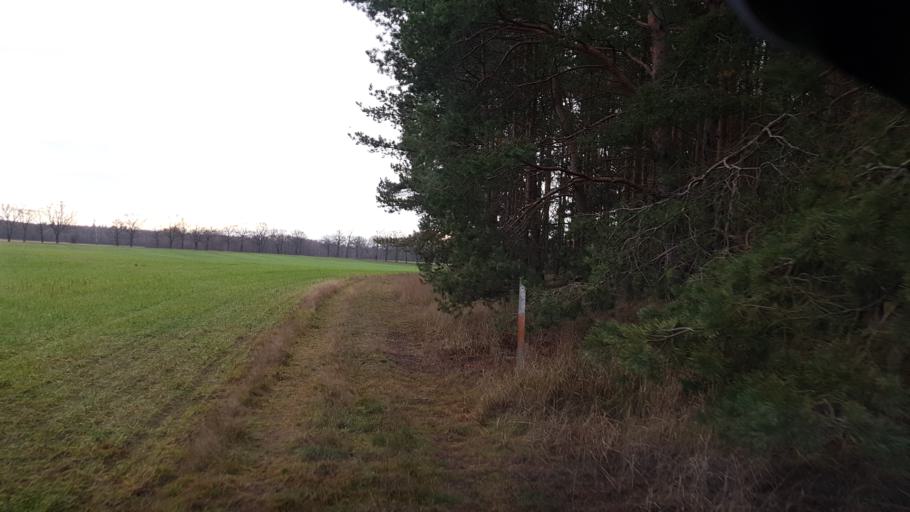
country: DE
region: Brandenburg
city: Altdobern
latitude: 51.6761
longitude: 14.0260
